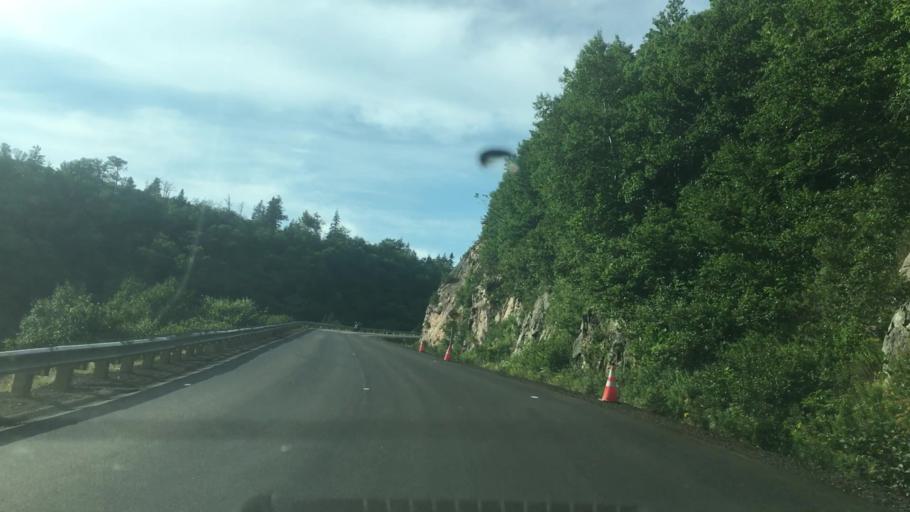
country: CA
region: Nova Scotia
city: Sydney Mines
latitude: 46.8202
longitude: -60.6529
